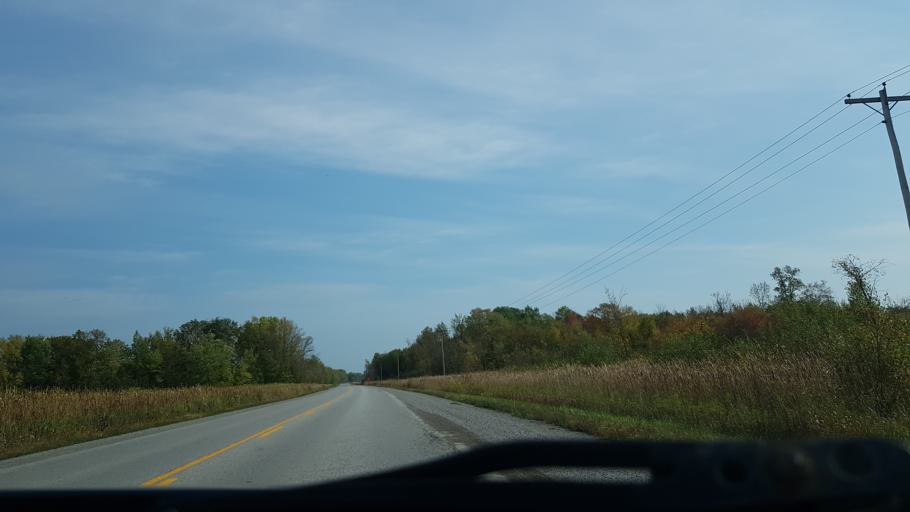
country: CA
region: Ontario
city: Orillia
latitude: 44.6473
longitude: -79.1339
